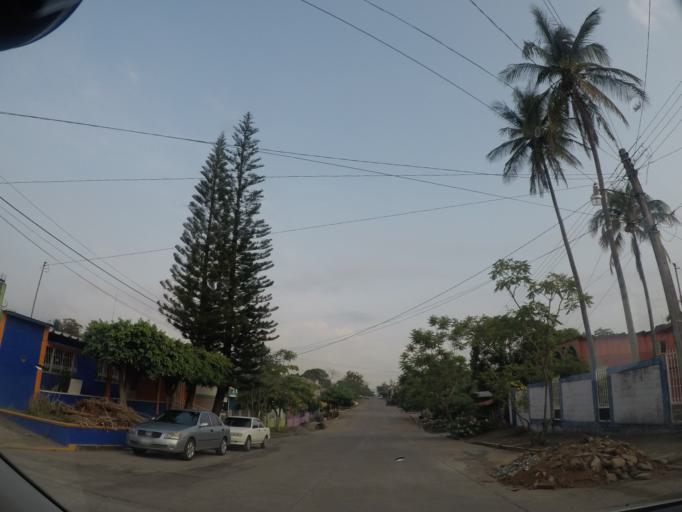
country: MX
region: Oaxaca
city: Matias Romero
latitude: 16.8722
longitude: -95.0387
